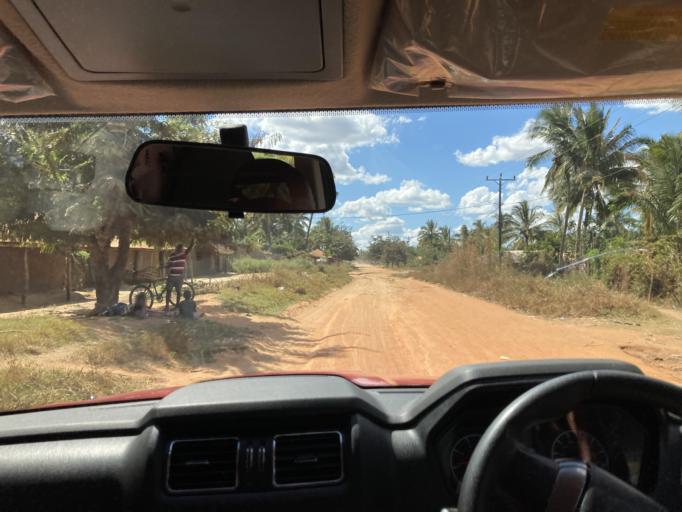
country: MZ
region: Cabo Delgado
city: Montepuez
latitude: -13.1443
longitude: 38.9932
